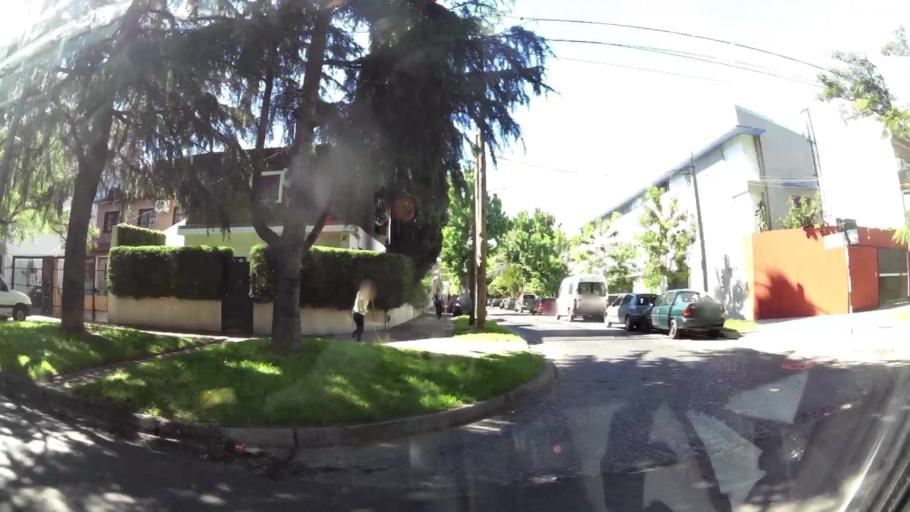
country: AR
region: Buenos Aires
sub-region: Partido de Vicente Lopez
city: Olivos
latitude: -34.5242
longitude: -58.4919
